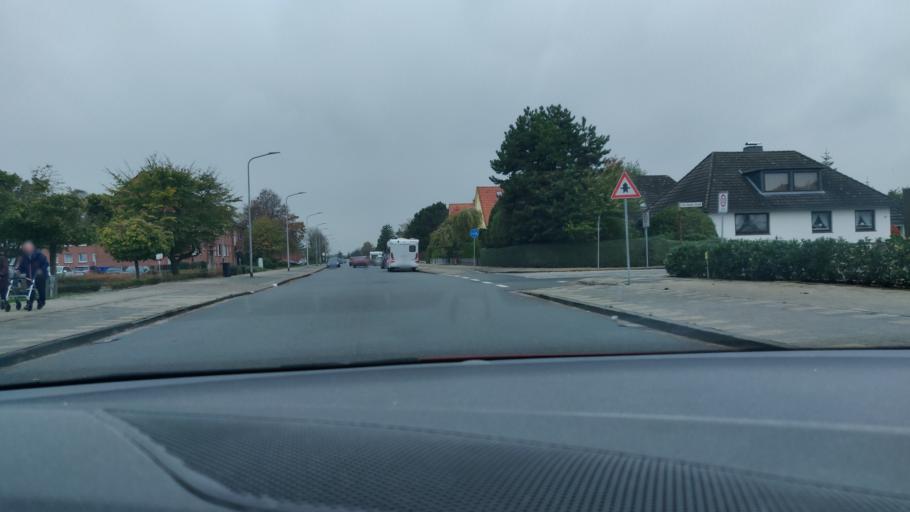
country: DE
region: Lower Saxony
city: Cuxhaven
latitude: 53.8701
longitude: 8.6844
